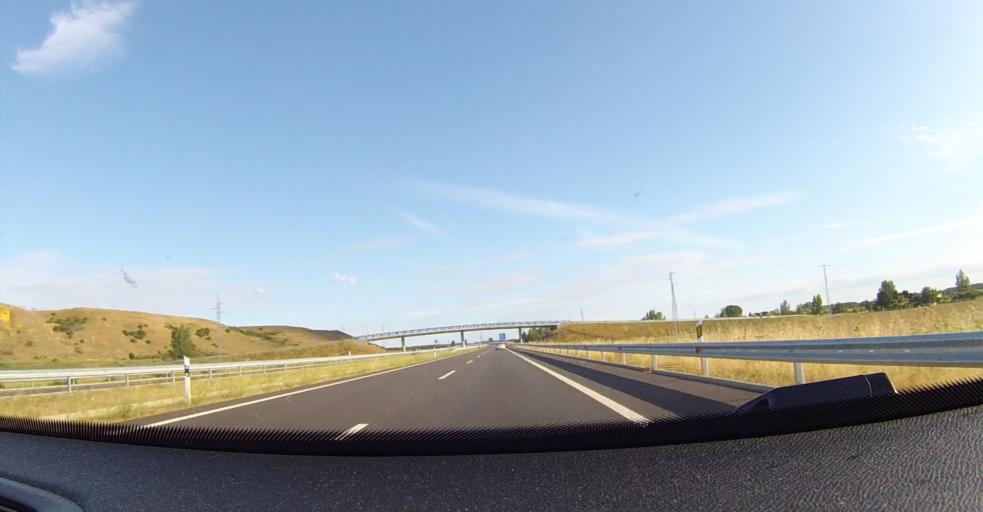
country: ES
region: Castille and Leon
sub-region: Provincia de Leon
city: Villasabariego
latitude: 42.5337
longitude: -5.4377
